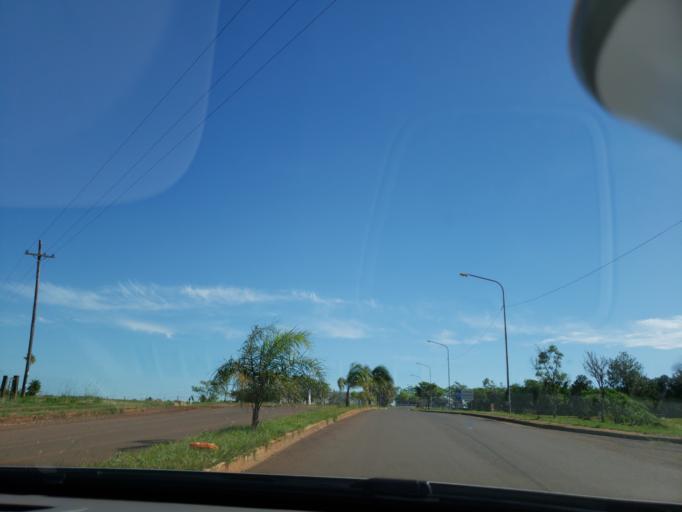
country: AR
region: Misiones
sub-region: Departamento de Capital
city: Posadas
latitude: -27.3905
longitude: -55.9623
